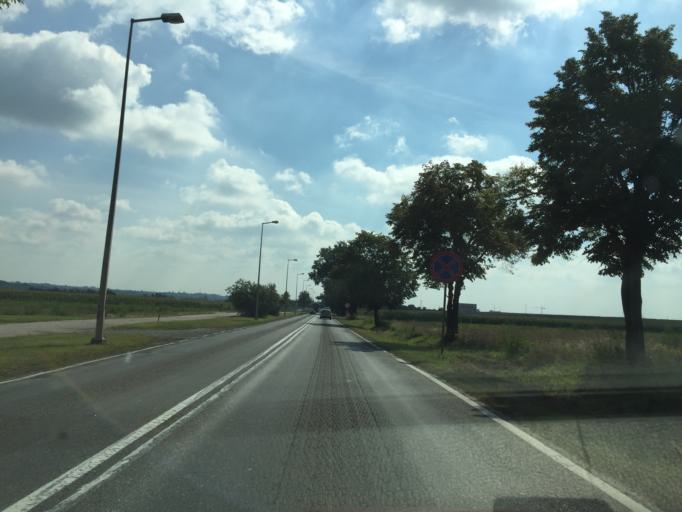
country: PL
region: Greater Poland Voivodeship
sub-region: Kalisz
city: Kalisz
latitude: 51.7690
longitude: 18.0428
